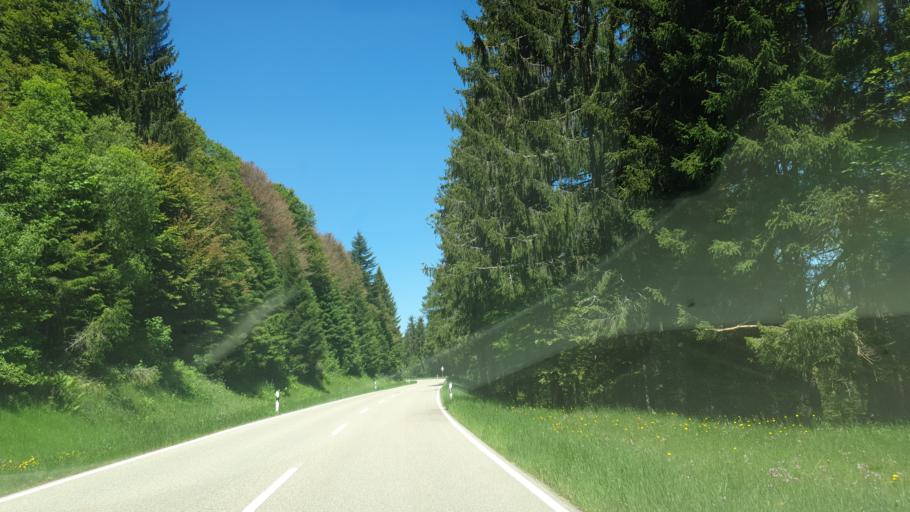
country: DE
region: Baden-Wuerttemberg
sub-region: Freiburg Region
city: Wieden
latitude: 47.8809
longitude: 7.9015
